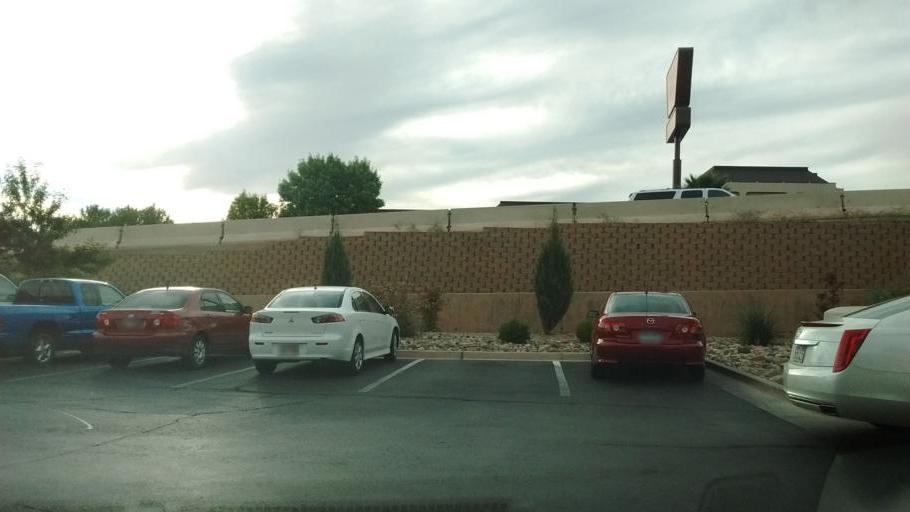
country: US
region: Utah
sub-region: Washington County
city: Saint George
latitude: 37.1086
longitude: -113.5542
